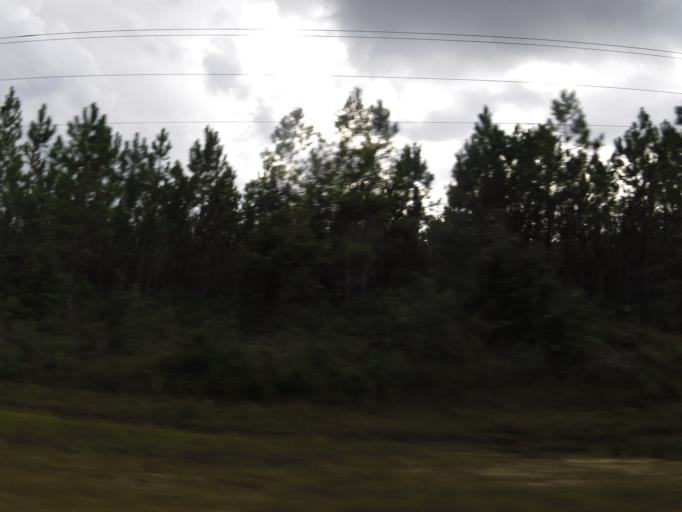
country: US
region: Florida
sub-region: Nassau County
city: Hilliard
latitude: 30.5666
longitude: -82.0439
